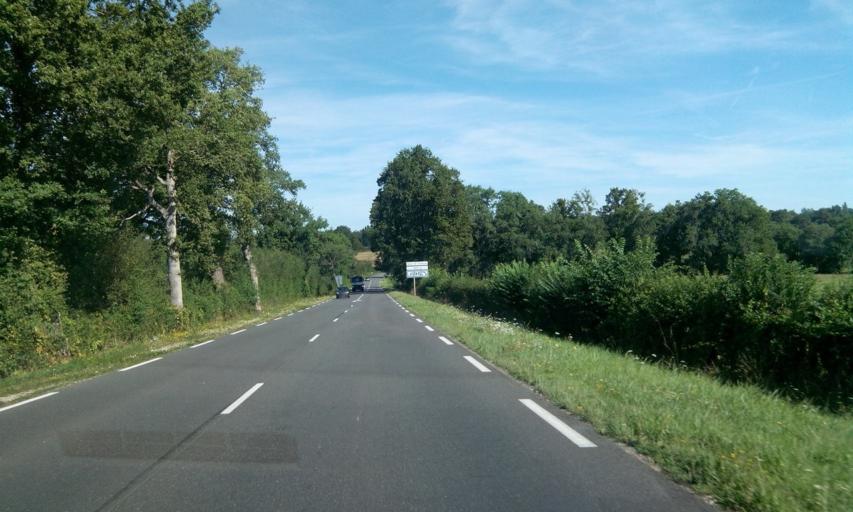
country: FR
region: Poitou-Charentes
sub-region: Departement de la Charente
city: Etagnac
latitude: 45.9256
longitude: 0.7408
